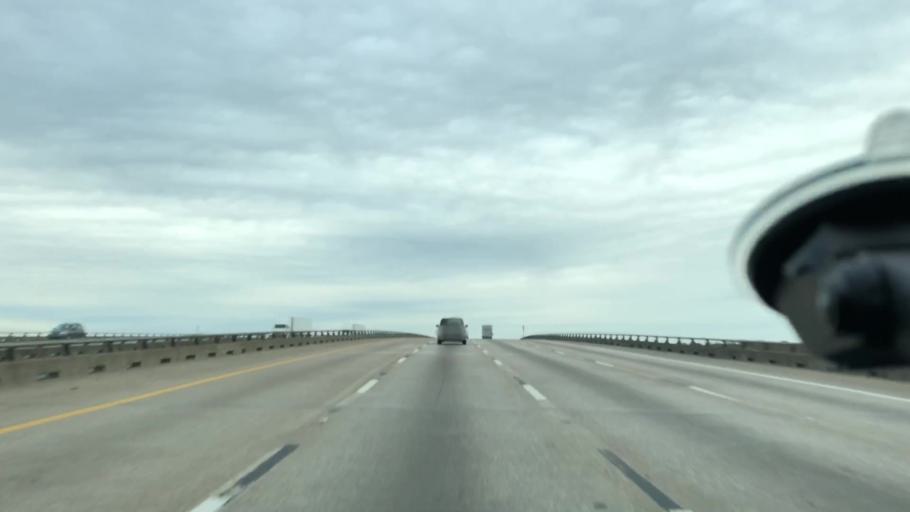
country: US
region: Texas
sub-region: Dallas County
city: Hutchins
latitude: 32.6772
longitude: -96.6914
